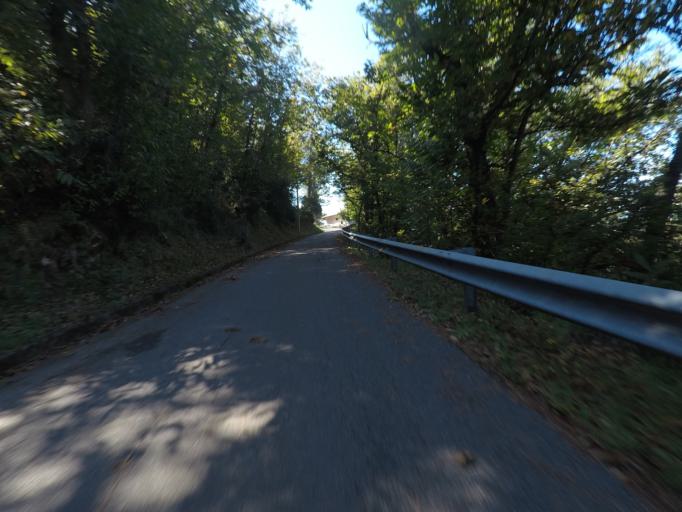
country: IT
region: Tuscany
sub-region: Provincia di Massa-Carrara
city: Montignoso
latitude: 44.0371
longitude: 10.1613
